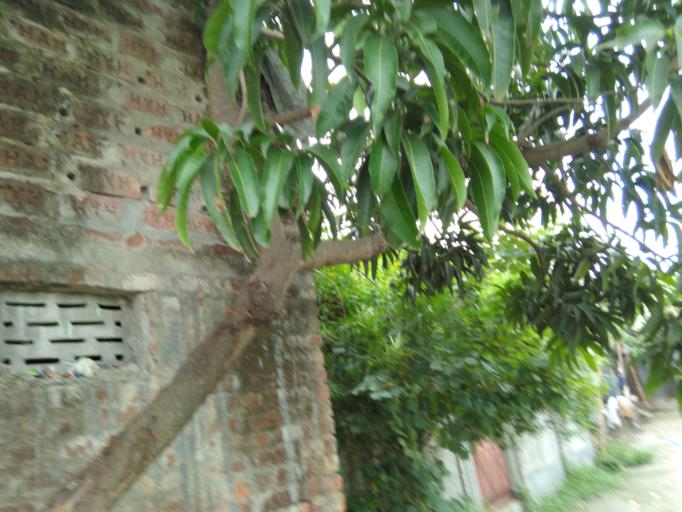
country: BD
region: Dhaka
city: Paltan
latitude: 23.7567
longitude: 90.4530
